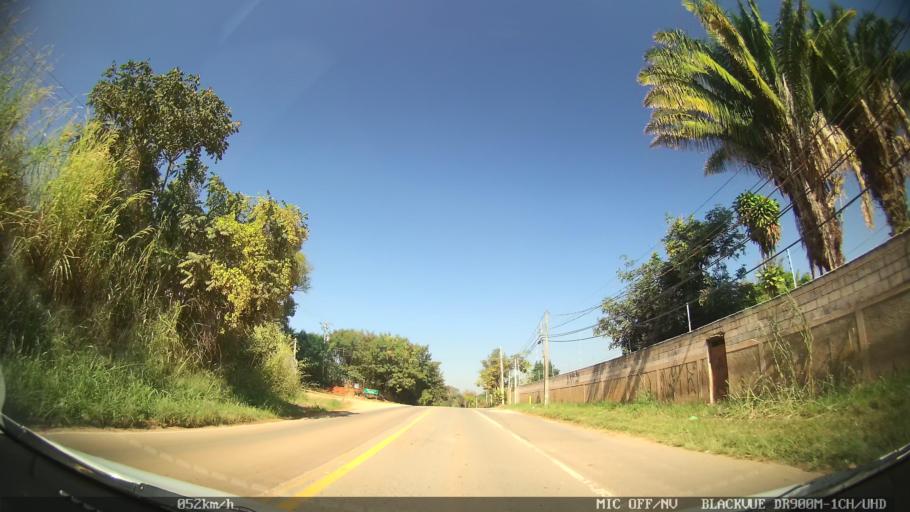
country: BR
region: Sao Paulo
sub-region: Campinas
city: Campinas
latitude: -22.9840
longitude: -47.0853
